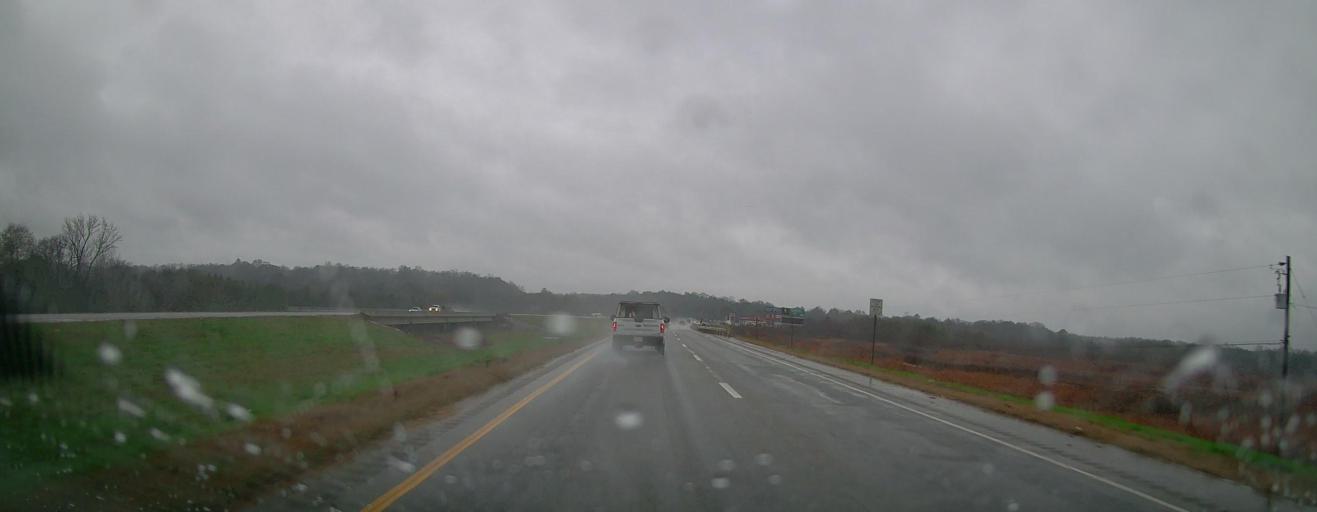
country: US
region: Alabama
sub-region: Autauga County
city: Prattville
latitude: 32.4173
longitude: -86.4099
